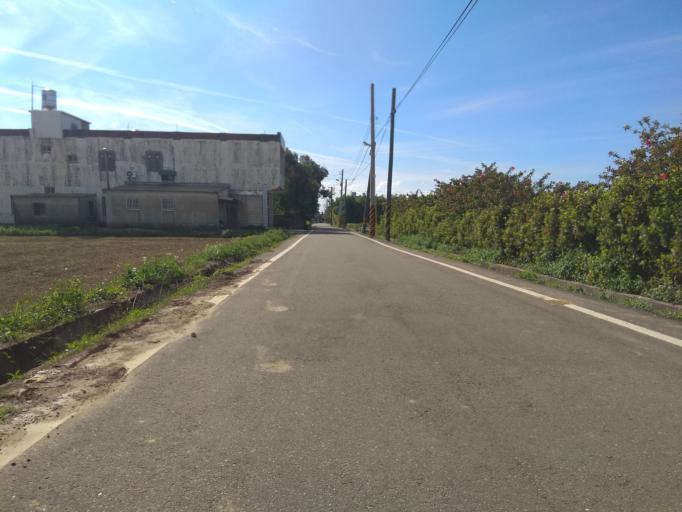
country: TW
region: Taiwan
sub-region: Hsinchu
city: Zhubei
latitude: 24.9906
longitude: 121.0407
